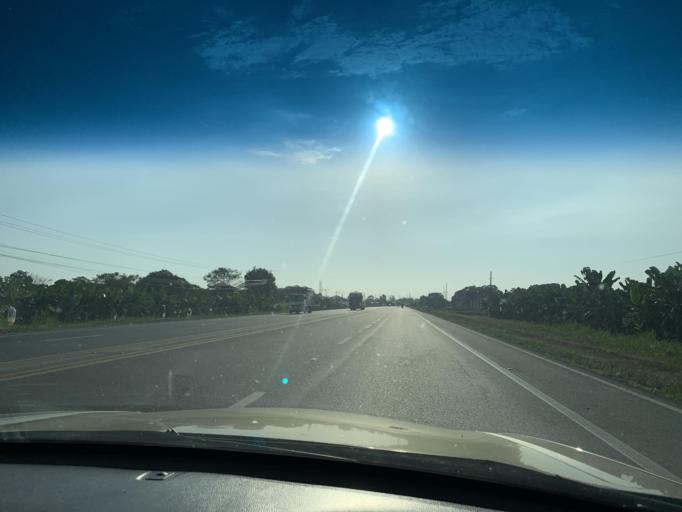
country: EC
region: Guayas
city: Yaguachi Nuevo
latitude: -2.2544
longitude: -79.6217
